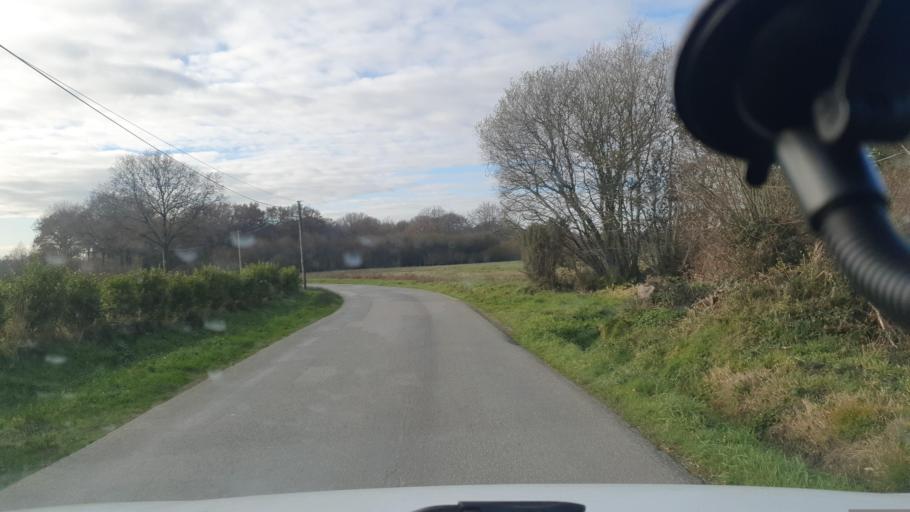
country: FR
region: Brittany
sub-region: Departement du Finistere
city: Briec
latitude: 48.1161
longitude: -4.0174
